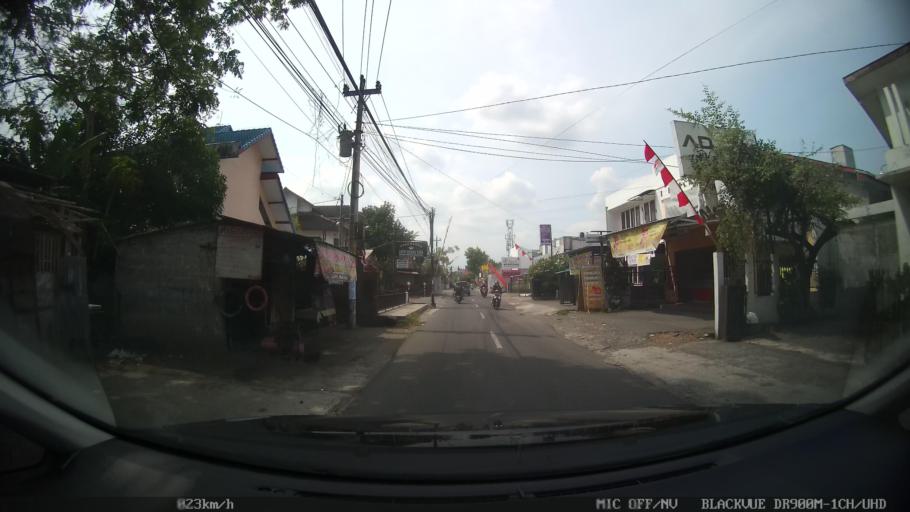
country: ID
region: Daerah Istimewa Yogyakarta
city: Depok
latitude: -7.8012
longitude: 110.4162
